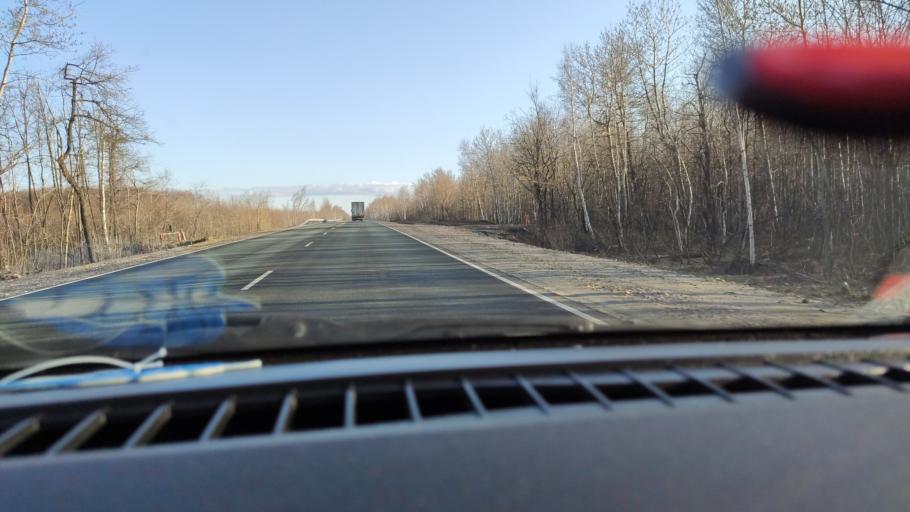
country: RU
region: Saratov
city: Alekseyevka
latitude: 52.4231
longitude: 48.0083
